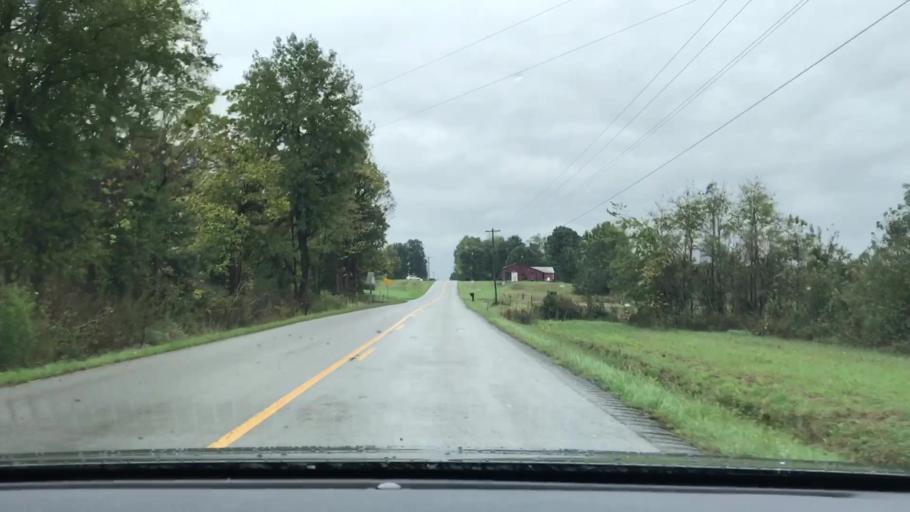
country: US
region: Kentucky
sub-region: McLean County
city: Calhoun
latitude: 37.4641
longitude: -87.2328
